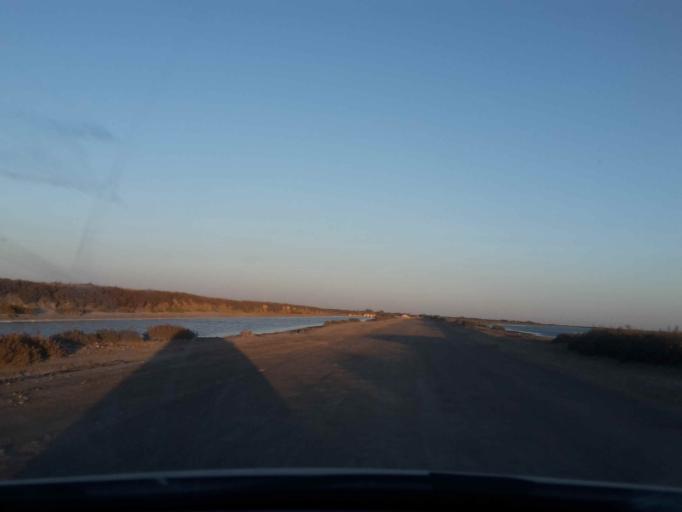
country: FR
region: Provence-Alpes-Cote d'Azur
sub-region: Departement des Bouches-du-Rhone
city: Port-Saint-Louis-du-Rhone
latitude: 43.4081
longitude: 4.6592
